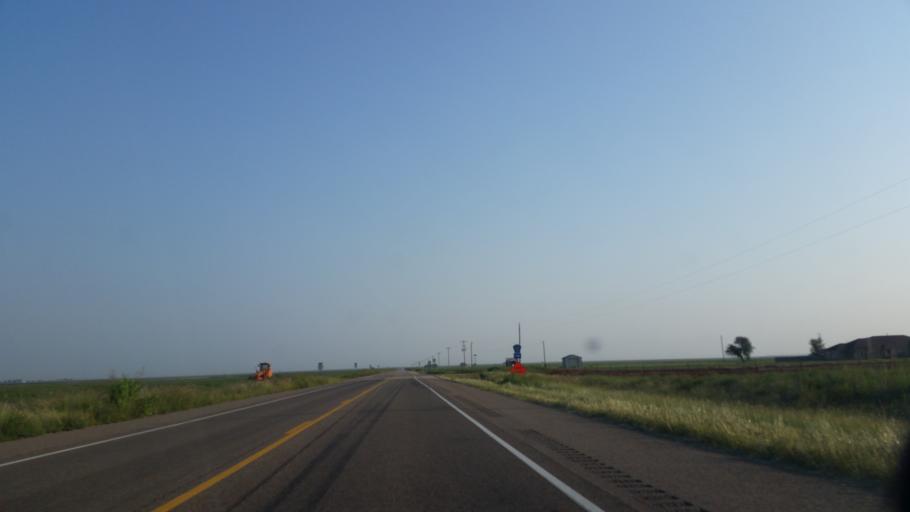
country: US
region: New Mexico
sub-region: Curry County
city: Clovis
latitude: 34.5782
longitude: -103.1964
